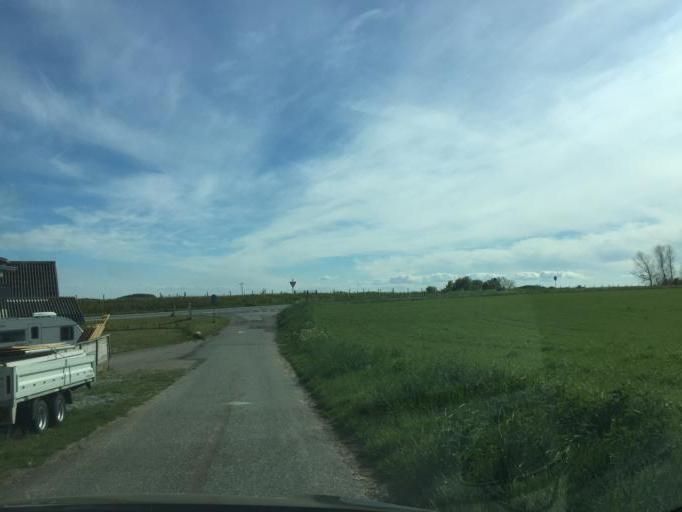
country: DK
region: South Denmark
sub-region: Fredericia Kommune
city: Taulov
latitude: 55.5294
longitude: 9.5651
